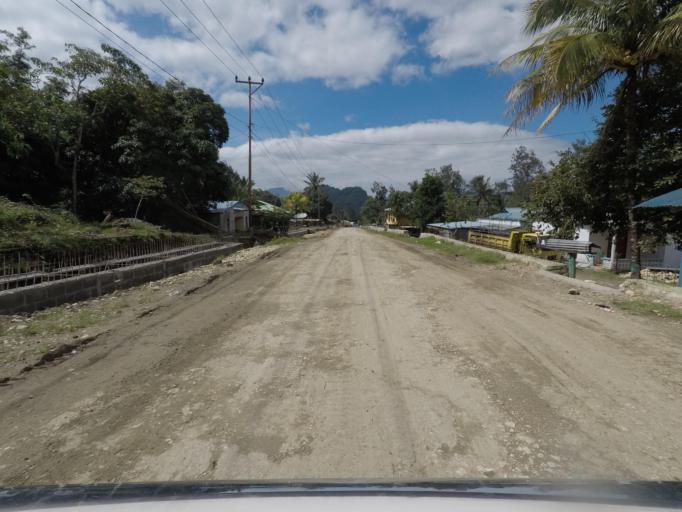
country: TL
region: Baucau
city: Venilale
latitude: -8.7390
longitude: 126.3784
